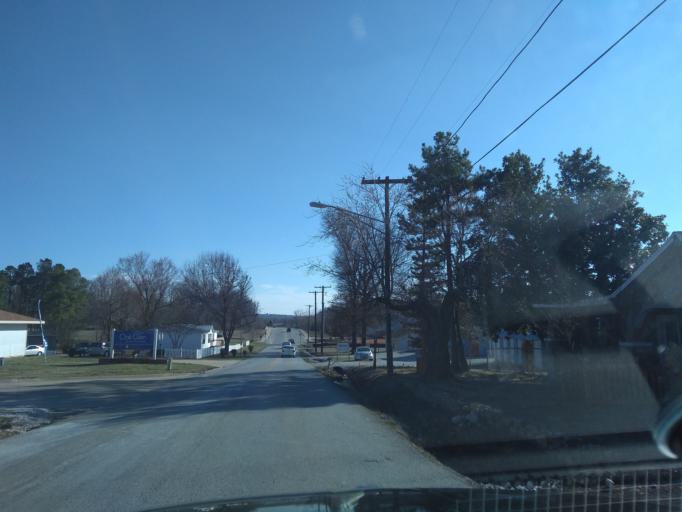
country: US
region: Arkansas
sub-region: Washington County
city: Johnson
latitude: 36.1309
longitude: -94.1630
